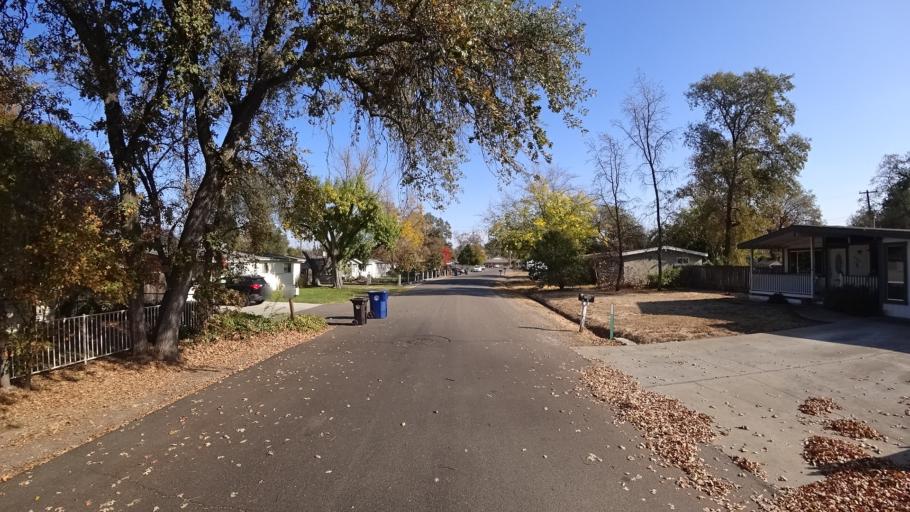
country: US
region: California
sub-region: Sacramento County
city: Citrus Heights
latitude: 38.6825
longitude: -121.2864
